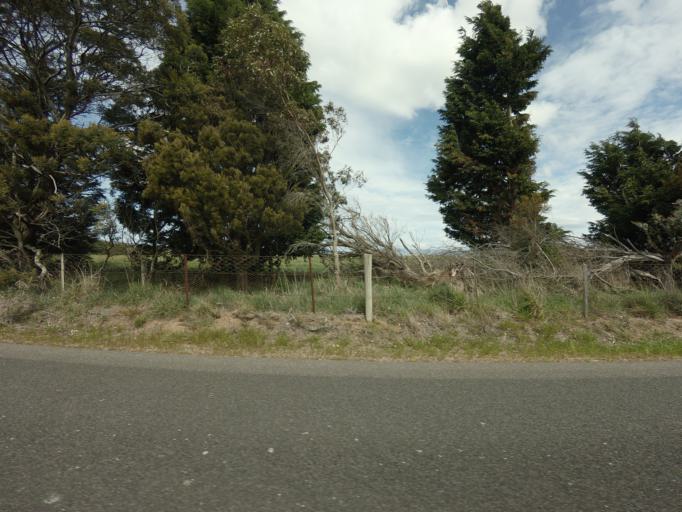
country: AU
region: Tasmania
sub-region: Northern Midlands
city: Longford
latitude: -41.6600
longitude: 147.1634
